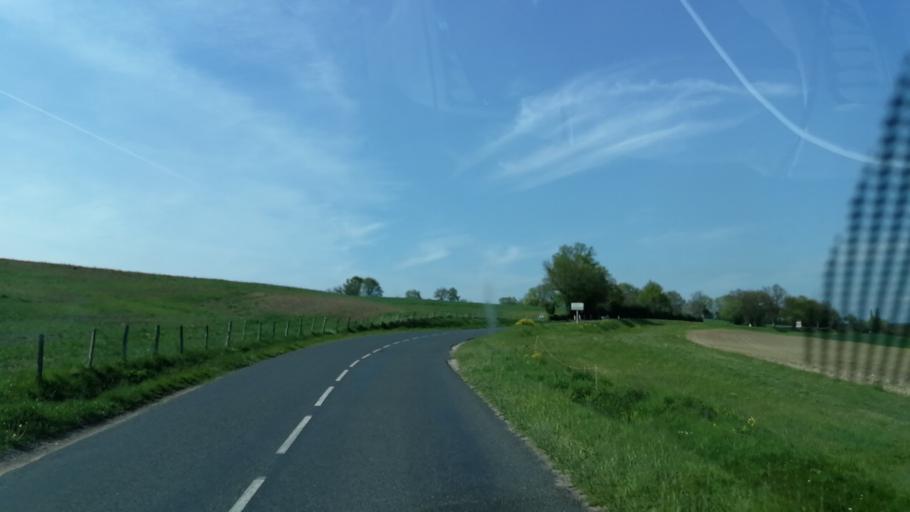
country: FR
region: Auvergne
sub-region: Departement de l'Allier
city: Saint-Gerand-le-Puy
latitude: 46.3575
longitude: 3.5770
